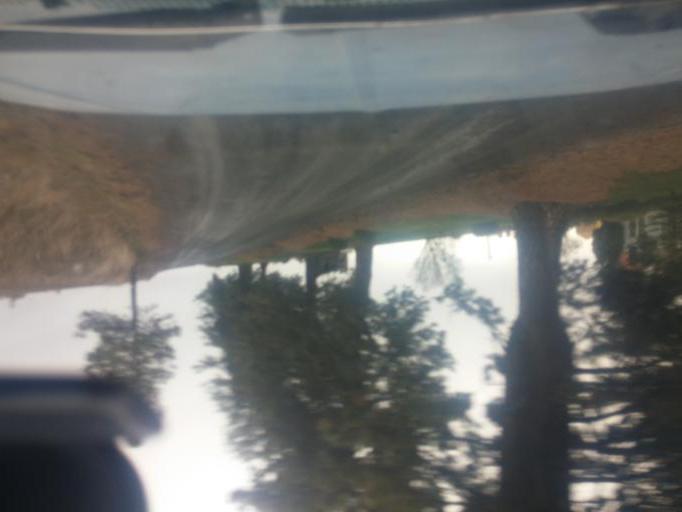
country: US
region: Idaho
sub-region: Latah County
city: Moscow
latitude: 46.9173
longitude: -116.8542
